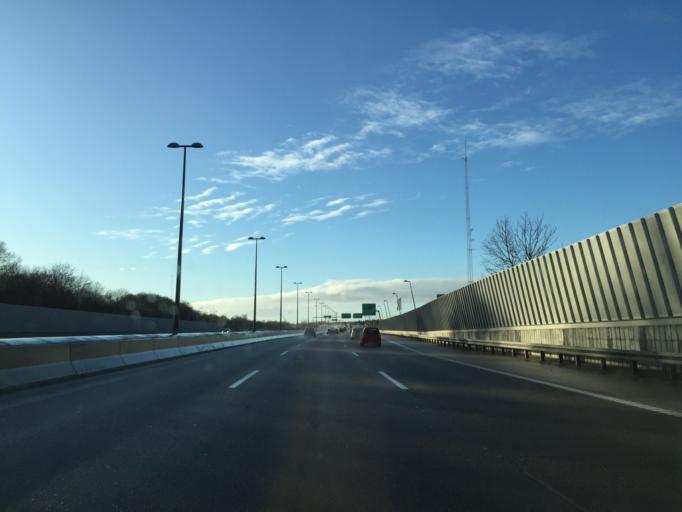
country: DK
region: Capital Region
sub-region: Rodovre Kommune
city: Rodovre
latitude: 55.6963
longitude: 12.4422
